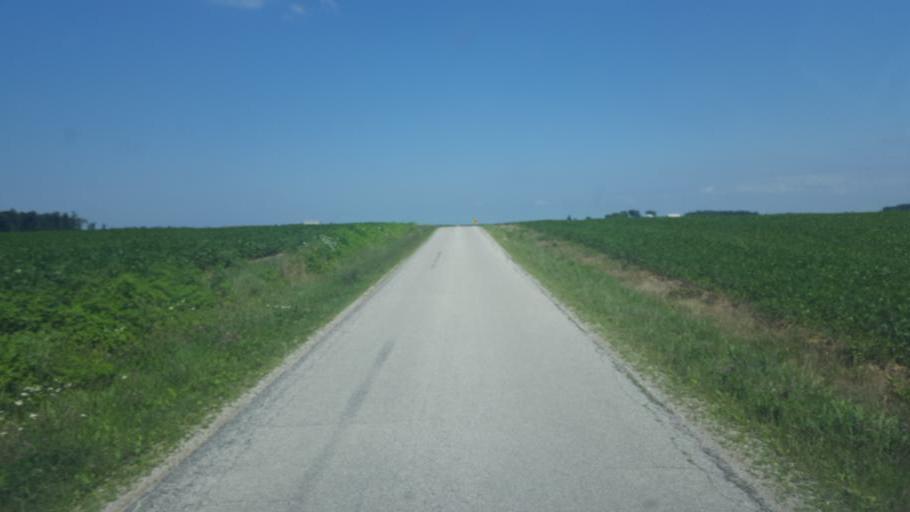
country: US
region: Ohio
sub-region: Huron County
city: Bellevue
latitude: 41.1458
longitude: -82.8380
